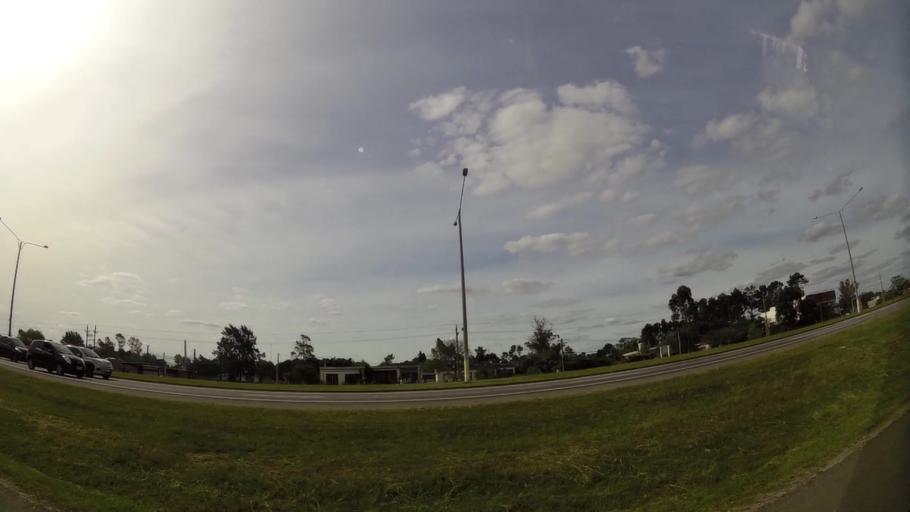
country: UY
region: Canelones
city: Empalme Olmos
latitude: -34.7772
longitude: -55.8508
